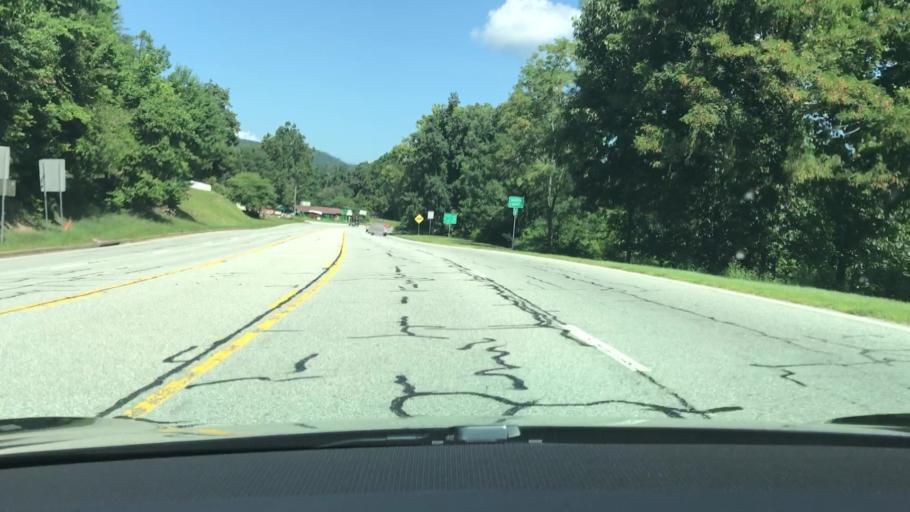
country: US
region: Georgia
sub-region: Rabun County
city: Clayton
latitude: 34.7357
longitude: -83.3905
